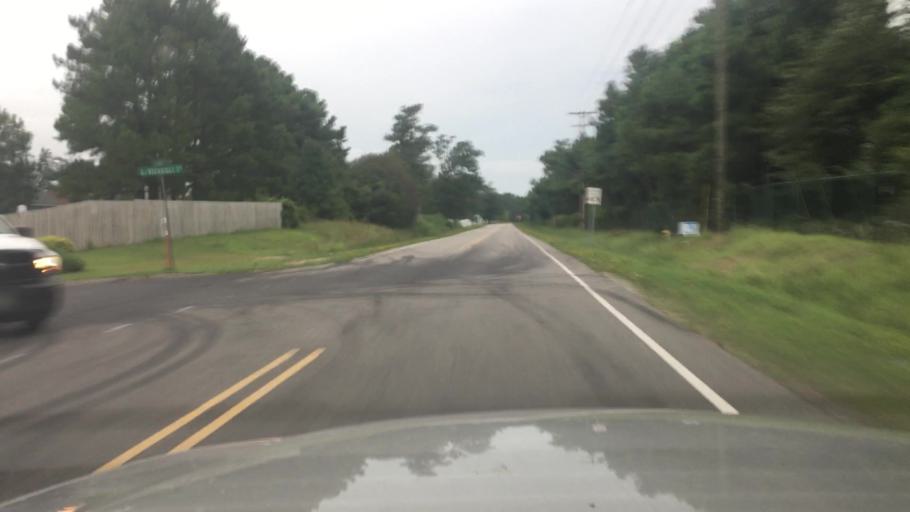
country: US
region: North Carolina
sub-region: Hoke County
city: Rockfish
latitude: 34.9927
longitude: -79.0235
